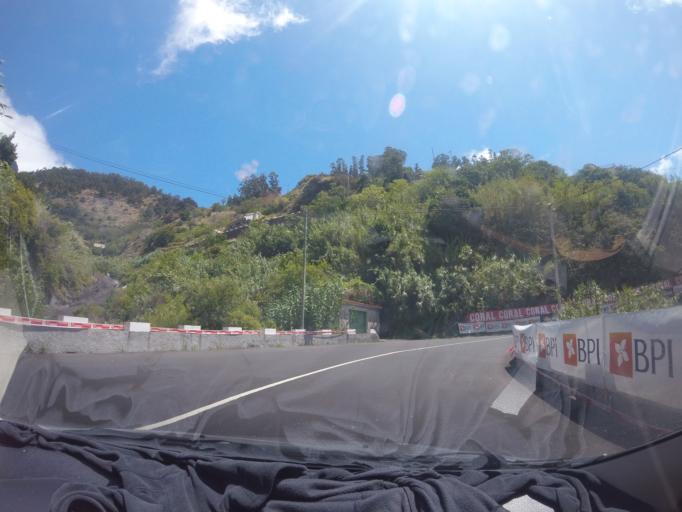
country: PT
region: Madeira
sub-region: Camara de Lobos
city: Curral das Freiras
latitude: 32.7330
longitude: -17.0273
